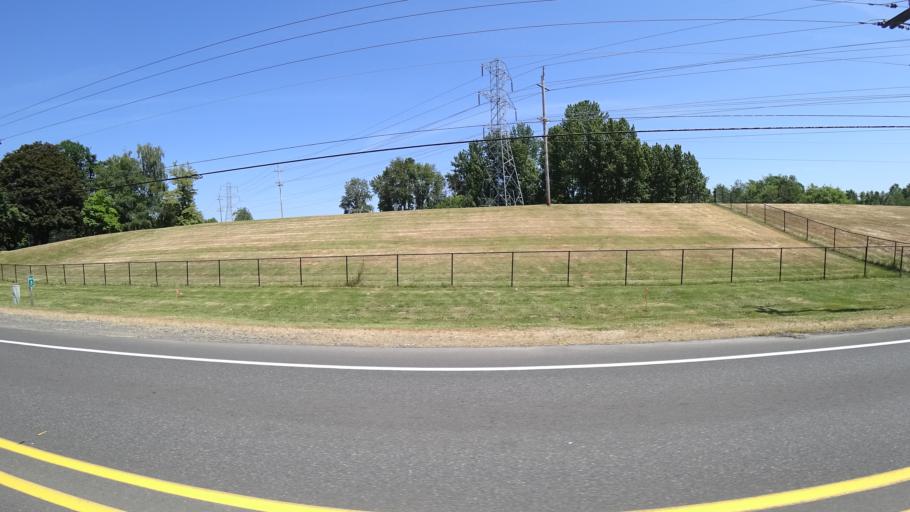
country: US
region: Oregon
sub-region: Multnomah County
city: Fairview
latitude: 45.5508
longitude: -122.4334
